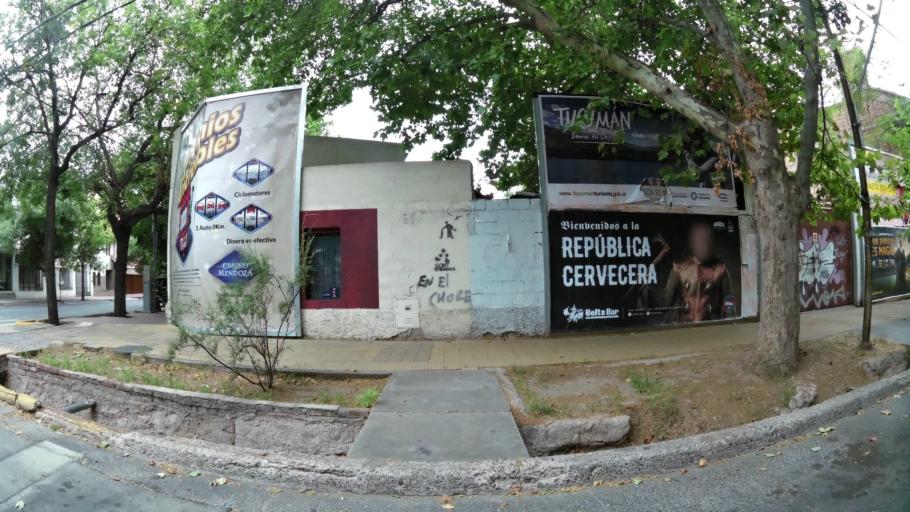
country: AR
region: Mendoza
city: Mendoza
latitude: -32.8995
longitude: -68.8515
